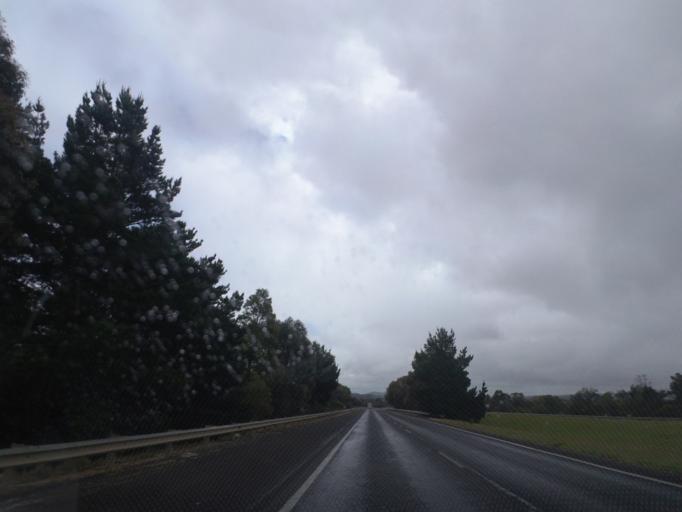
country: AU
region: Victoria
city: Black Hill
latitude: -37.5299
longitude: 143.8711
